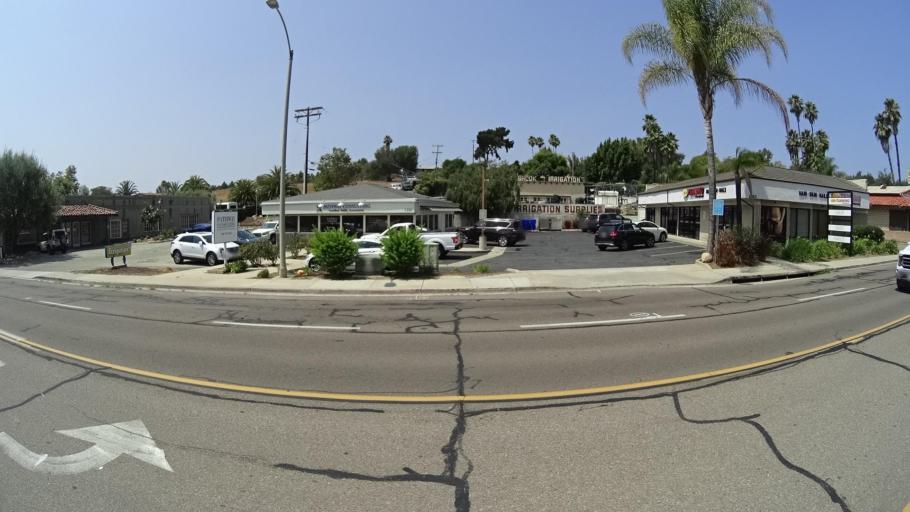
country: US
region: California
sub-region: San Diego County
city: Fallbrook
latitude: 33.3640
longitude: -117.2493
